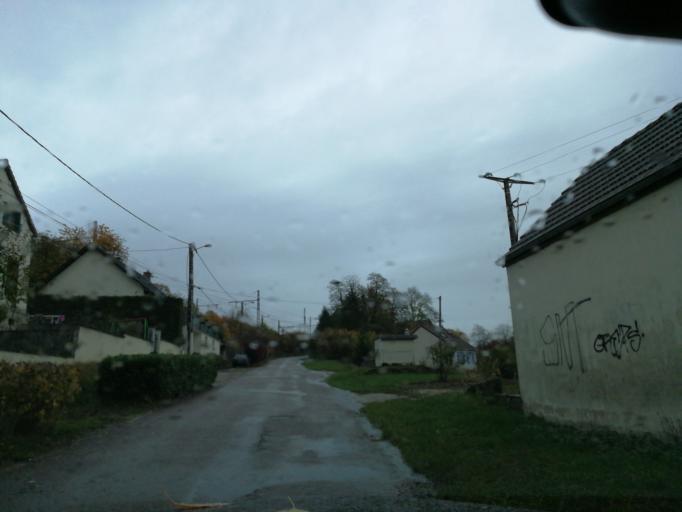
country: FR
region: Bourgogne
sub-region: Departement de la Cote-d'Or
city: Fleurey-sur-Ouche
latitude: 47.3276
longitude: 4.8062
